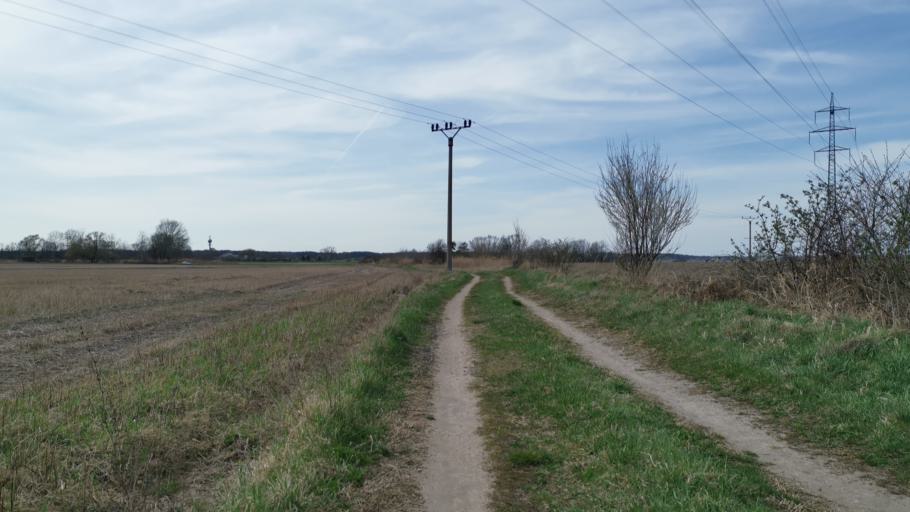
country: CZ
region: South Moravian
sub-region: Okres Breclav
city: Lanzhot
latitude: 48.6947
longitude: 17.0311
